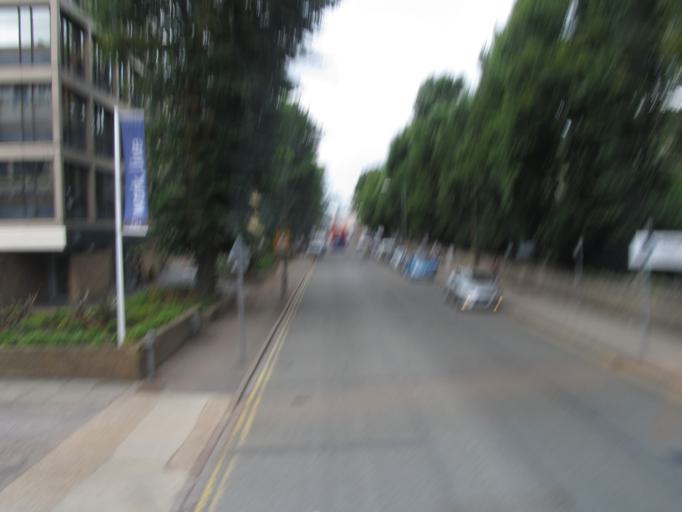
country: GB
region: England
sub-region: Cambridgeshire
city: Cambridge
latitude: 52.1946
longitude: 0.1349
